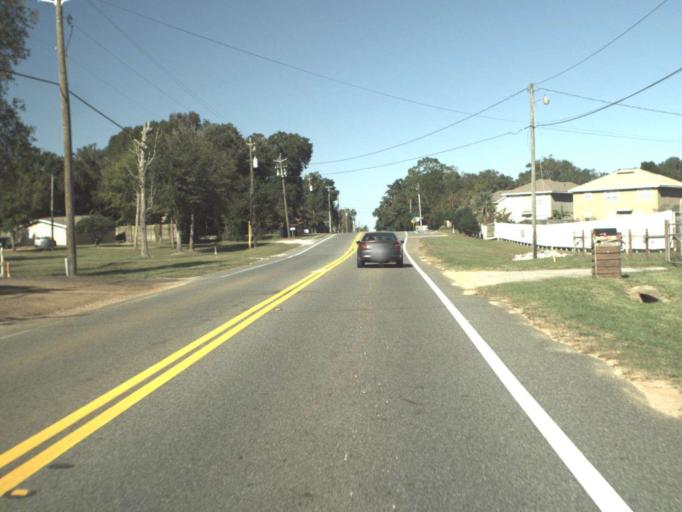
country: US
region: Florida
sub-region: Escambia County
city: Bellview
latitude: 30.4830
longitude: -87.3128
